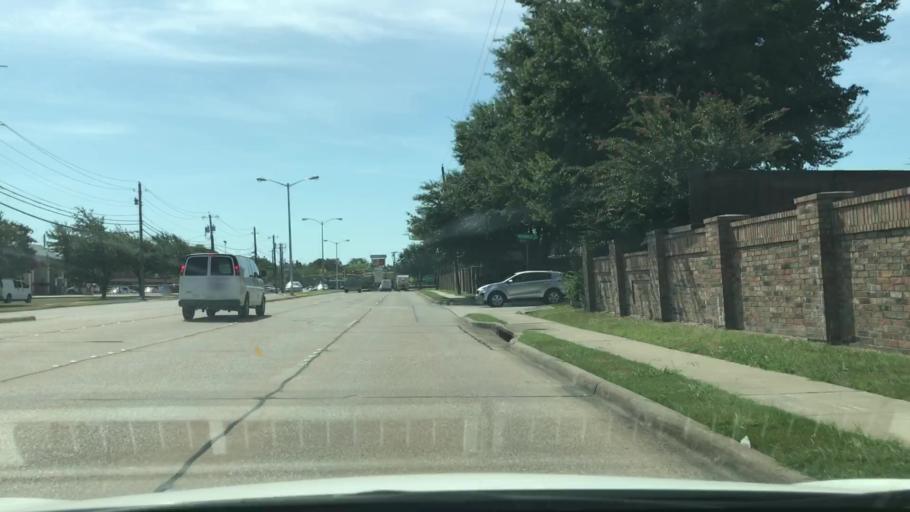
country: US
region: Texas
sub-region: Dallas County
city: Garland
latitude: 32.9418
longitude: -96.6420
